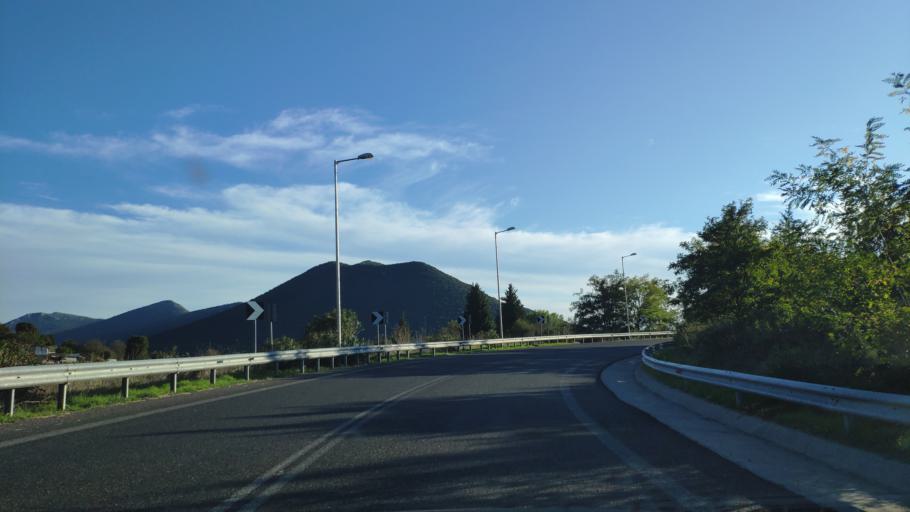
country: GR
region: Peloponnese
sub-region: Nomos Arkadias
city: Tripoli
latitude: 37.5904
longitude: 22.4380
